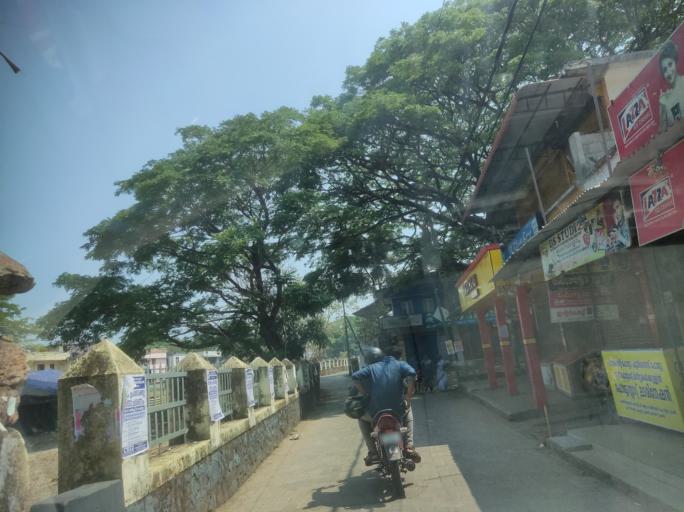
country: IN
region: Kerala
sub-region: Alappuzha
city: Shertallai
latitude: 9.6854
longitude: 76.3412
